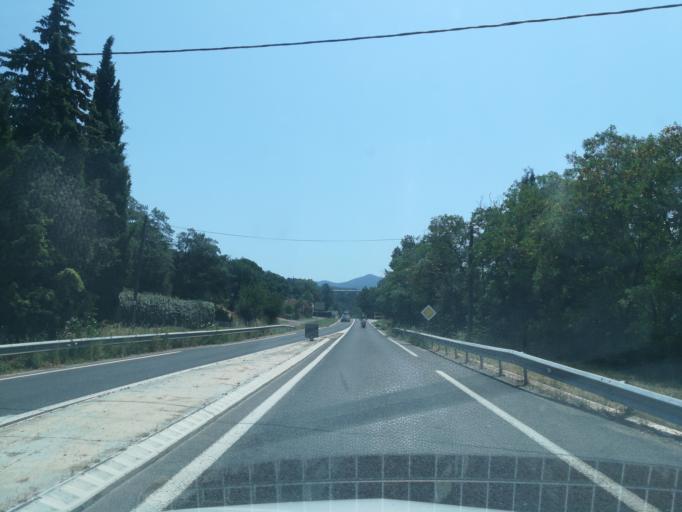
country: FR
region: Languedoc-Roussillon
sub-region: Departement des Pyrenees-Orientales
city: Maureillas-las-Illas
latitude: 42.4914
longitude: 2.8318
